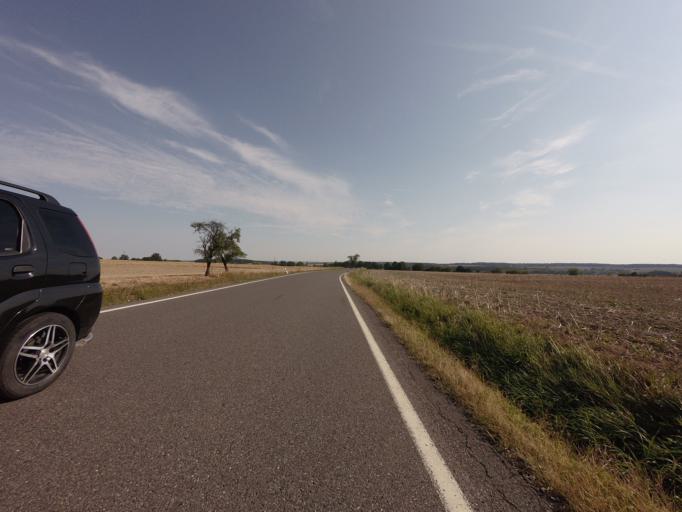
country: CZ
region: Jihocesky
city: Bernartice
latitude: 49.3354
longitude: 14.3630
